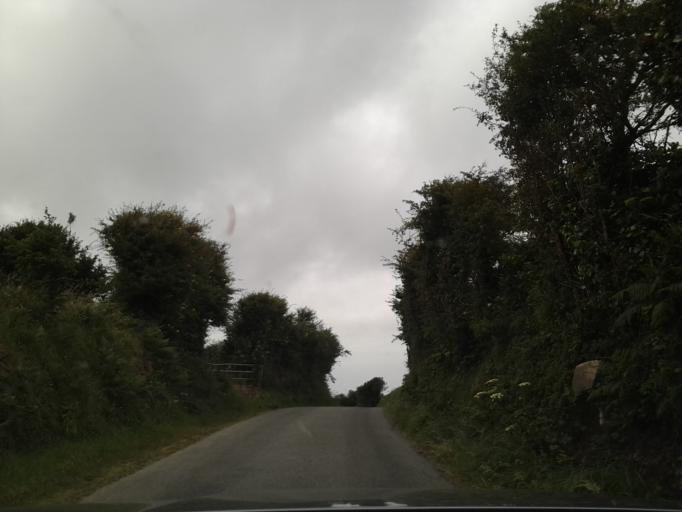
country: FR
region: Lower Normandy
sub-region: Departement de la Manche
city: Beaumont-Hague
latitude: 49.6854
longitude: -1.8687
